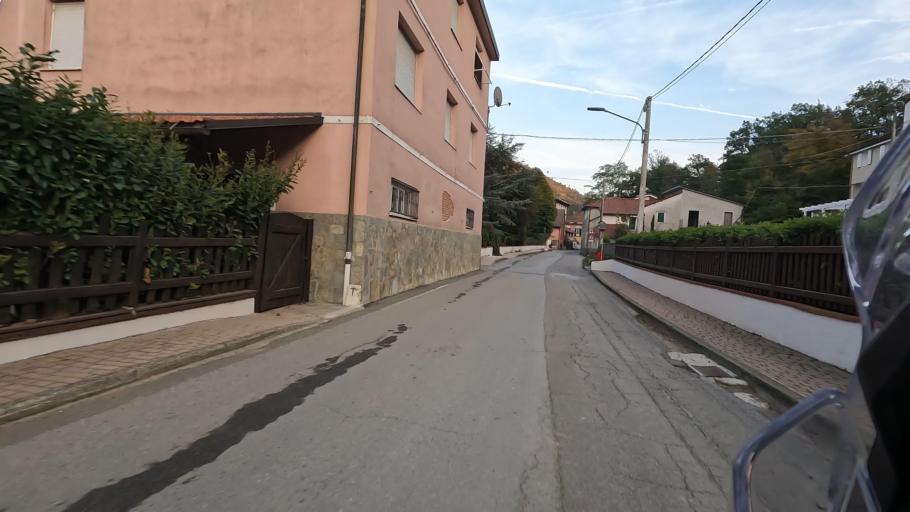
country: IT
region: Liguria
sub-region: Provincia di Savona
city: Pontinvrea
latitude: 44.4459
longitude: 8.4325
